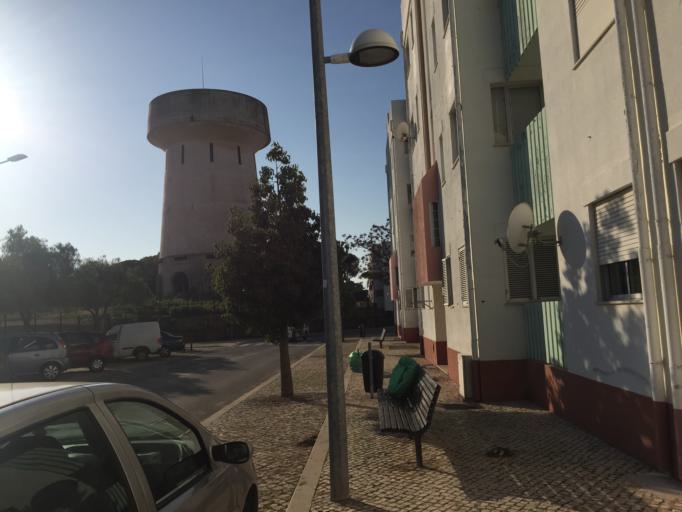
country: PT
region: Faro
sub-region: Vila Real de Santo Antonio
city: Vila Real de Santo Antonio
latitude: 37.1917
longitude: -7.4224
